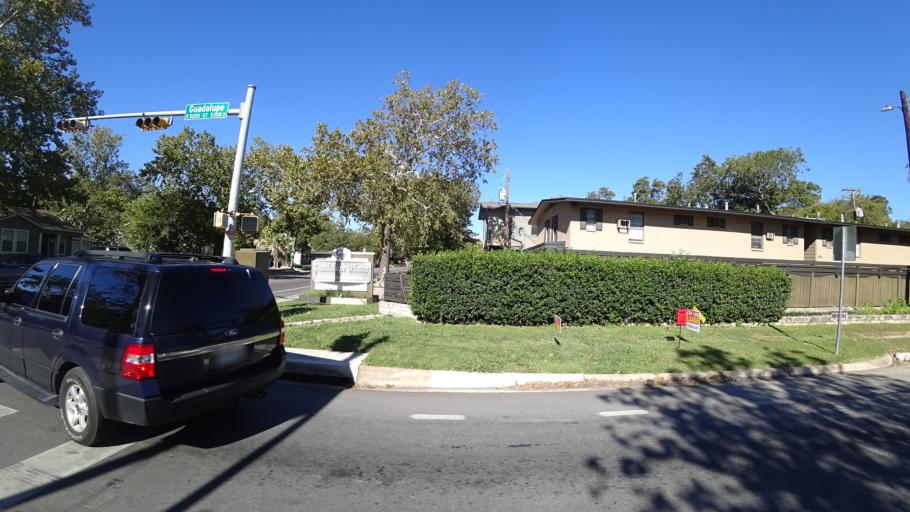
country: US
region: Texas
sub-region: Travis County
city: Austin
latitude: 30.3200
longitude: -97.7269
